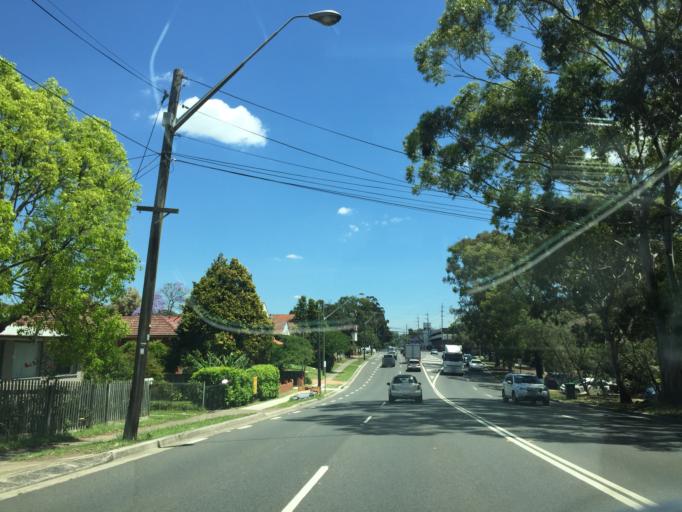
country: AU
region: New South Wales
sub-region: Ryde
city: Denistone
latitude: -33.7919
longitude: 151.0849
